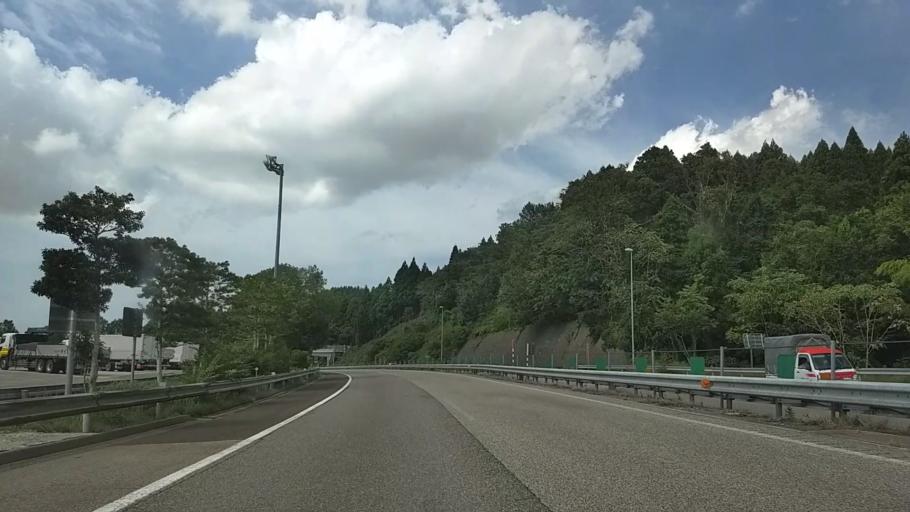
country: JP
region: Ishikawa
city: Tsubata
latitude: 36.6048
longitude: 136.7210
